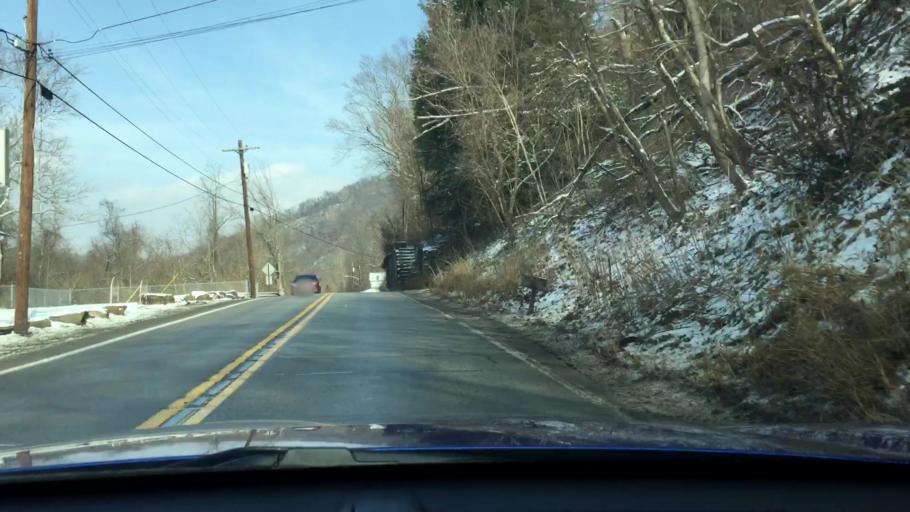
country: US
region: Pennsylvania
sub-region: Allegheny County
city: Clairton
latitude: 40.2883
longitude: -79.8666
